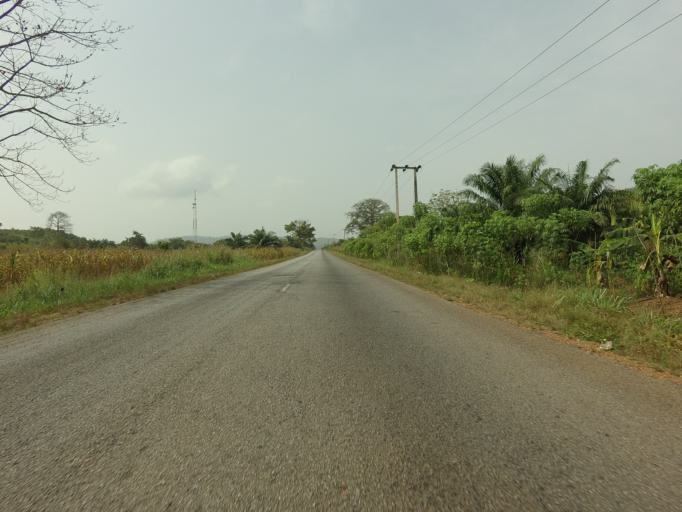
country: GH
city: Akropong
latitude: 6.3075
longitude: 0.1470
